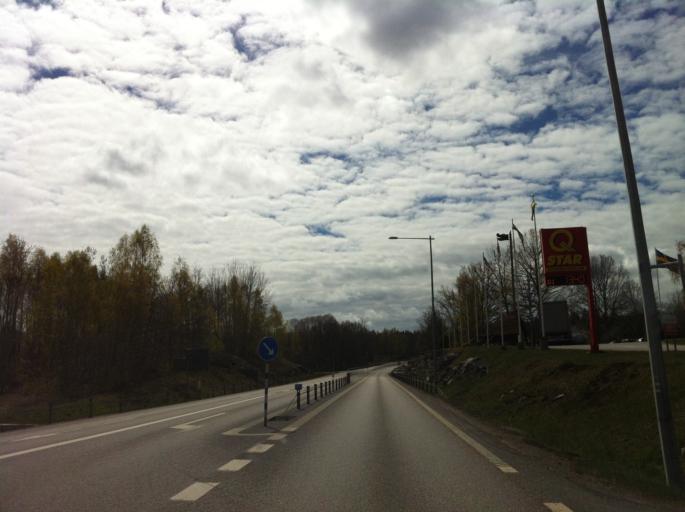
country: SE
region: OEstergoetland
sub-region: Valdemarsviks Kommun
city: Valdemarsvik
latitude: 58.1658
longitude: 16.5491
